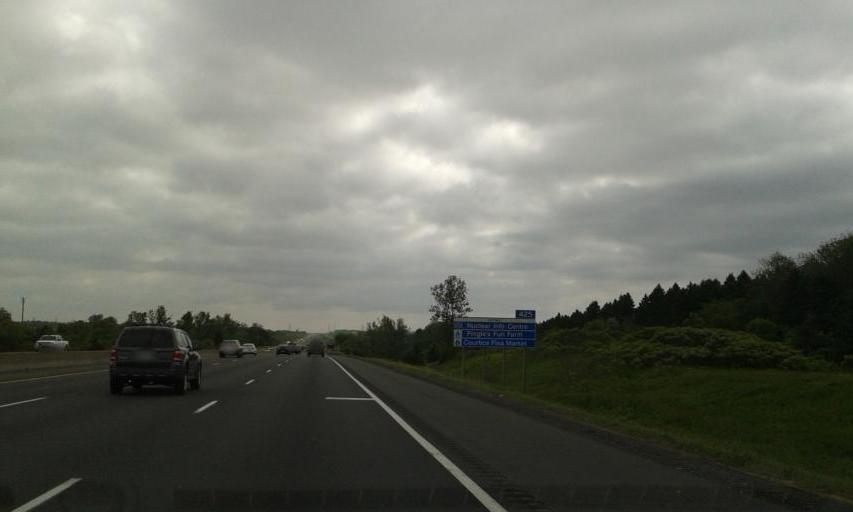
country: CA
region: Ontario
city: Oshawa
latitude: 43.8755
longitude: -78.7876
